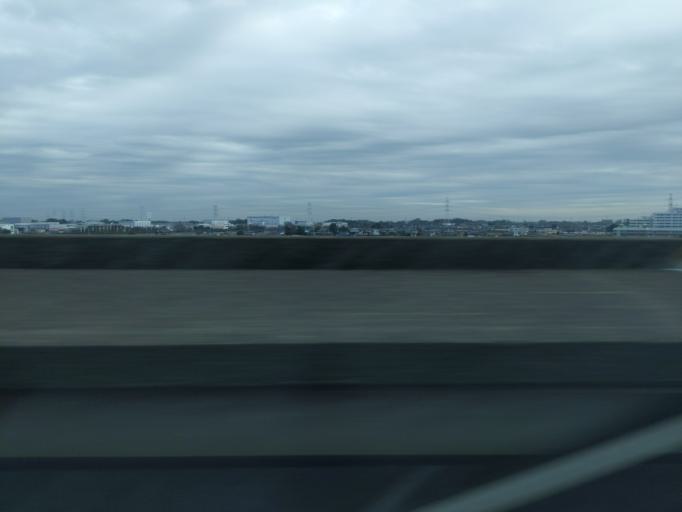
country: JP
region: Saitama
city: Kurihashi
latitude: 36.1213
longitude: 139.7128
